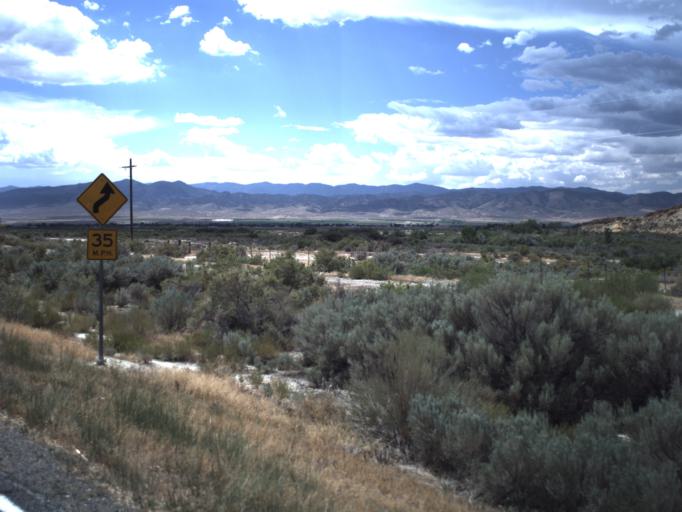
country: US
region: Utah
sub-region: Sanpete County
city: Centerfield
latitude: 39.1387
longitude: -111.7709
